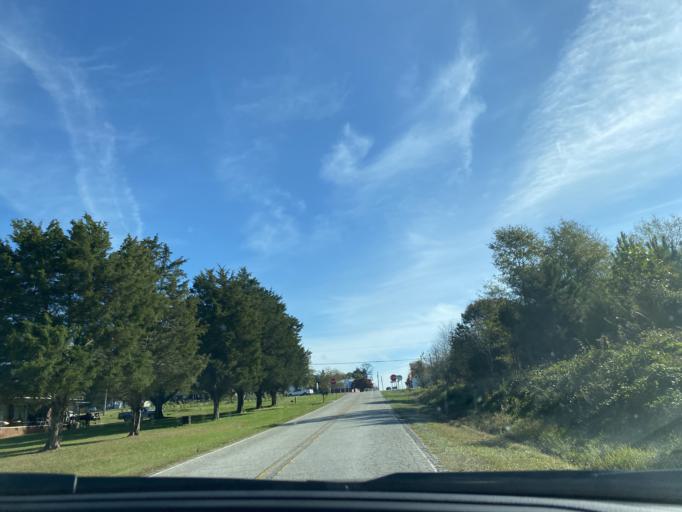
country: US
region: South Carolina
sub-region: Spartanburg County
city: Mayo
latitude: 35.0915
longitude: -81.8094
